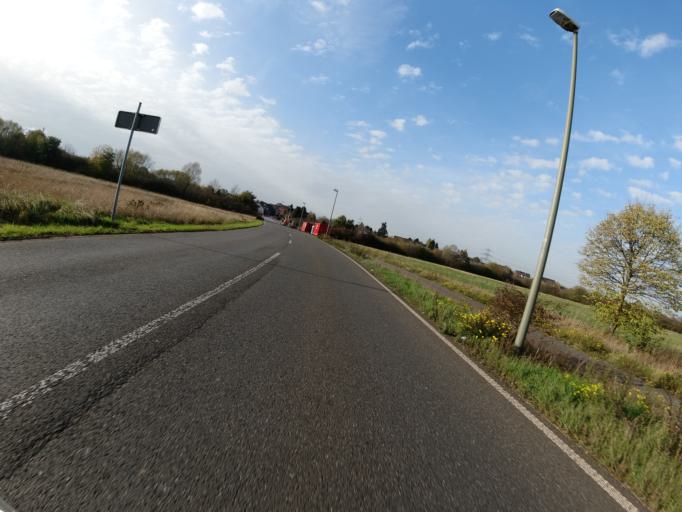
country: DE
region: North Rhine-Westphalia
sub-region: Regierungsbezirk Dusseldorf
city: Hochfeld
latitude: 51.3870
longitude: 6.6880
